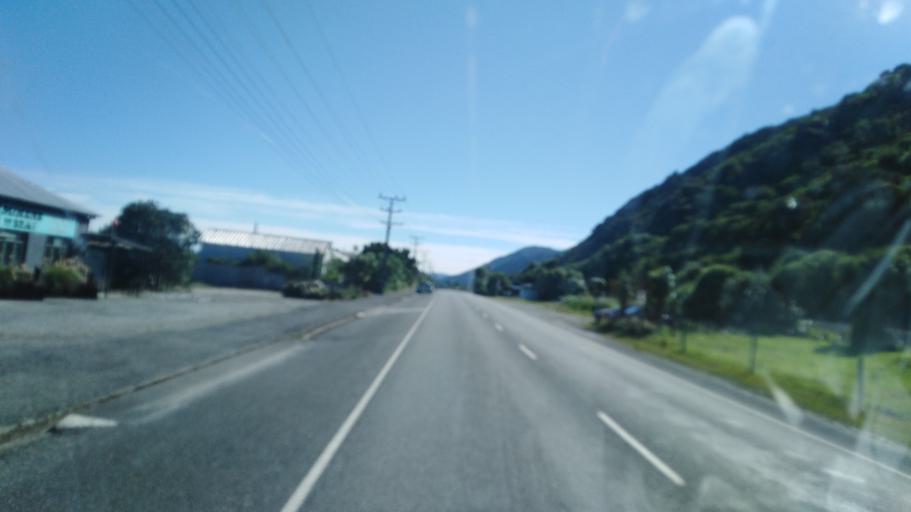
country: NZ
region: West Coast
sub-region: Buller District
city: Westport
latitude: -41.6258
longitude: 171.8573
